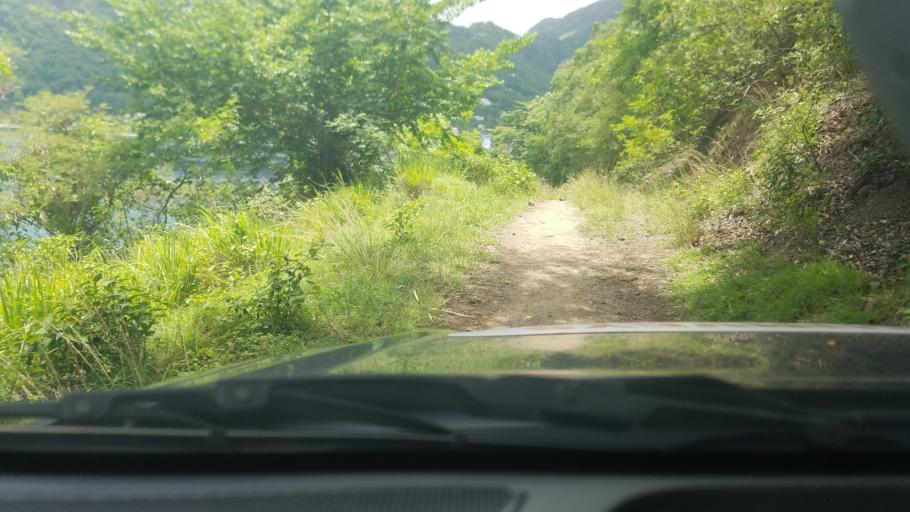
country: LC
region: Soufriere
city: Soufriere
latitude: 13.8488
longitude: -61.0620
